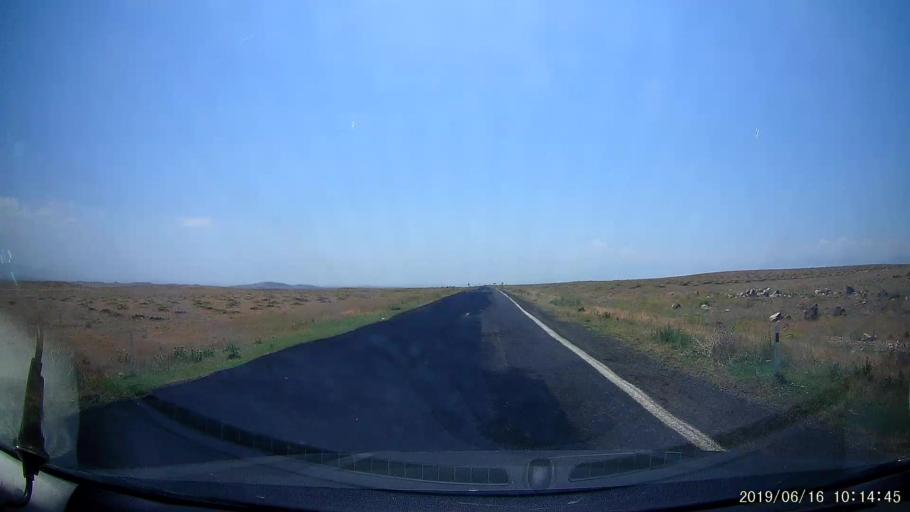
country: TR
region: Igdir
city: Tuzluca
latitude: 40.1821
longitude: 43.6691
